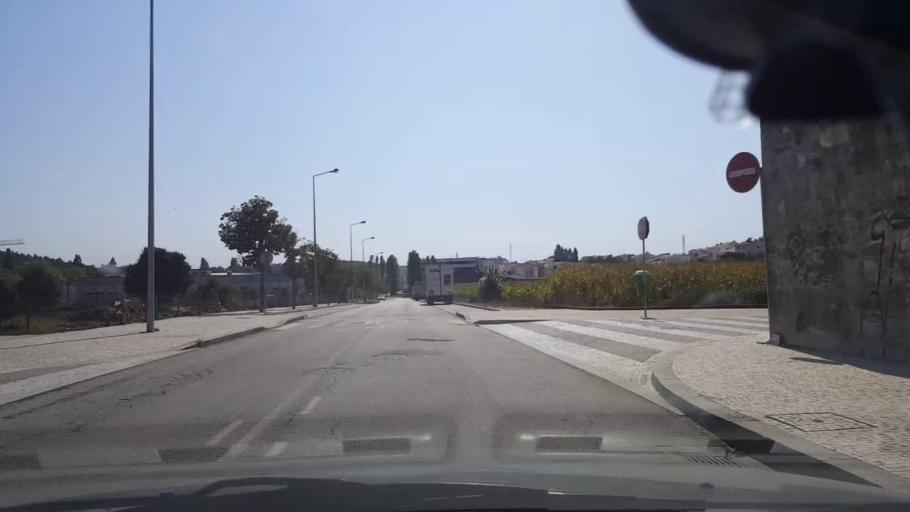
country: PT
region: Porto
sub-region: Vila do Conde
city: Vila do Conde
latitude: 41.3616
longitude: -8.7325
